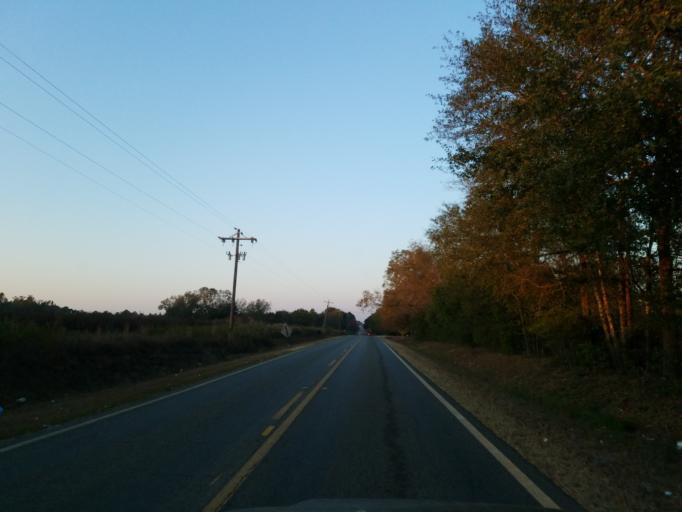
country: US
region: Georgia
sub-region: Ben Hill County
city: Fitzgerald
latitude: 31.6880
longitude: -83.3852
